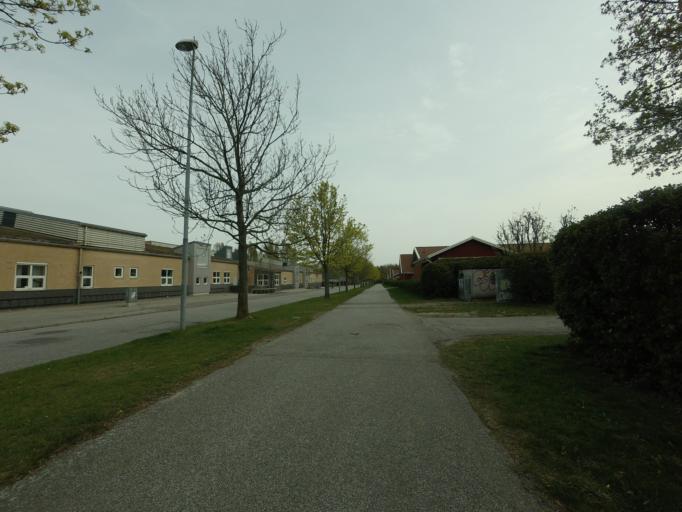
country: SE
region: Skane
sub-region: Lunds Kommun
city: Lund
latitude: 55.7244
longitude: 13.1670
